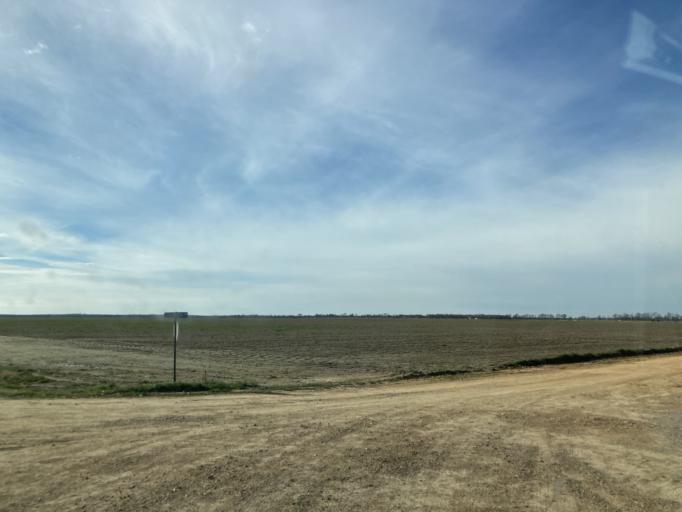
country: US
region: Mississippi
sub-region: Humphreys County
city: Belzoni
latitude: 33.0233
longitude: -90.6231
